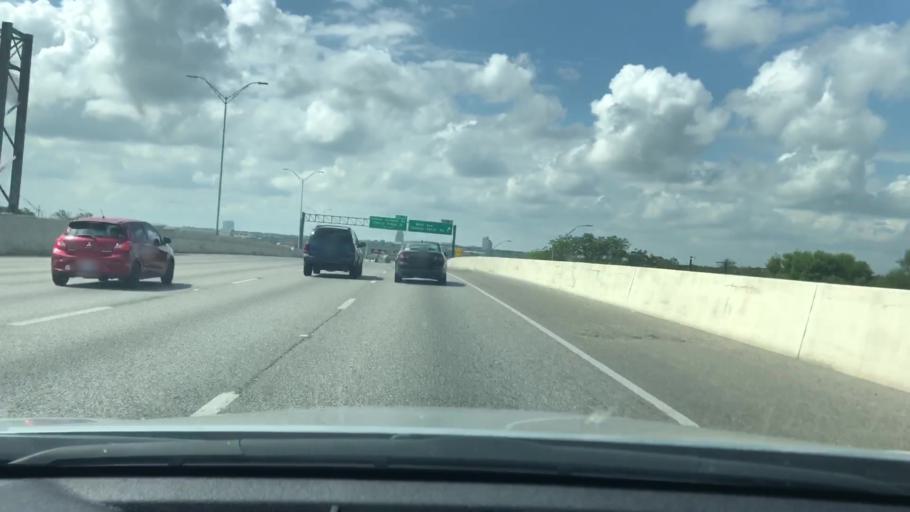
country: US
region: Texas
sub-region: Bexar County
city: Castle Hills
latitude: 29.5201
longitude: -98.5188
